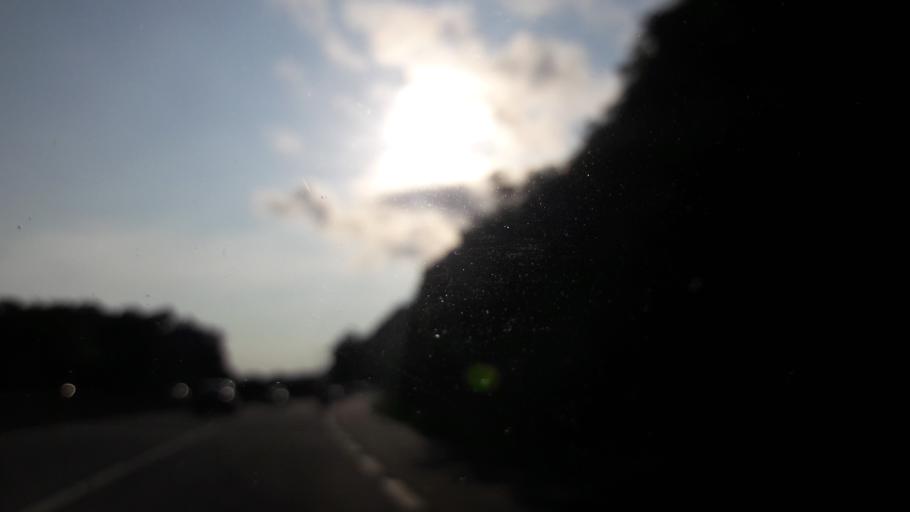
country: BR
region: Sao Paulo
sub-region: Mongagua
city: Mongagua
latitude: -24.0894
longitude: -46.6136
